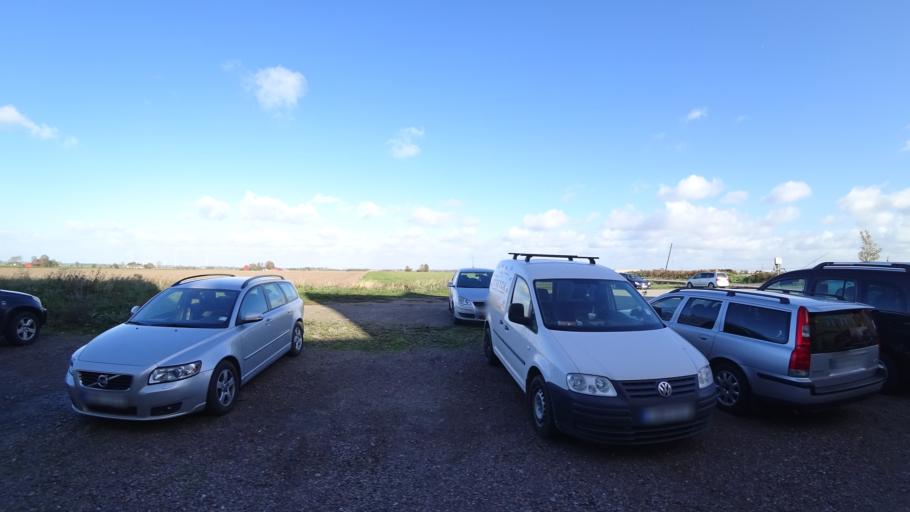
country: SE
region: Skane
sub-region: Staffanstorps Kommun
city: Hjaerup
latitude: 55.6759
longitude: 13.1356
